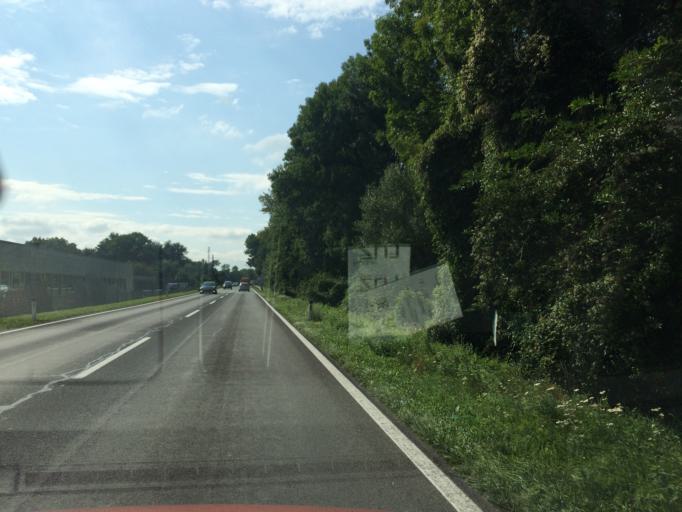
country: AT
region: Upper Austria
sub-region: Politischer Bezirk Linz-Land
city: Traun
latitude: 48.2108
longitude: 14.2495
